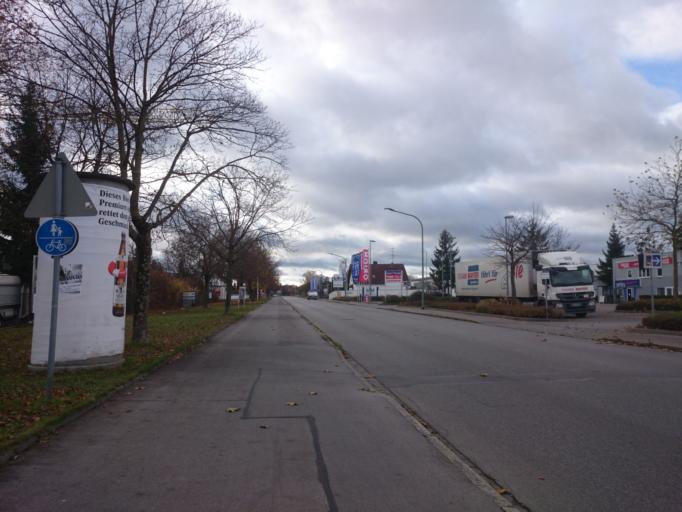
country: DE
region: Bavaria
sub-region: Swabia
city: Konigsbrunn
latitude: 48.2909
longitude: 10.8903
